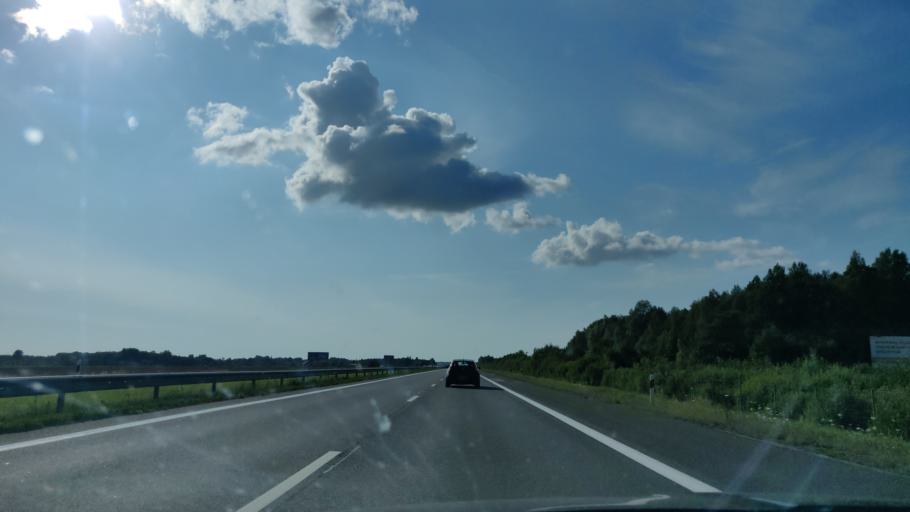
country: LT
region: Klaipedos apskritis
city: Gargzdai
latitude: 55.7180
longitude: 21.4430
